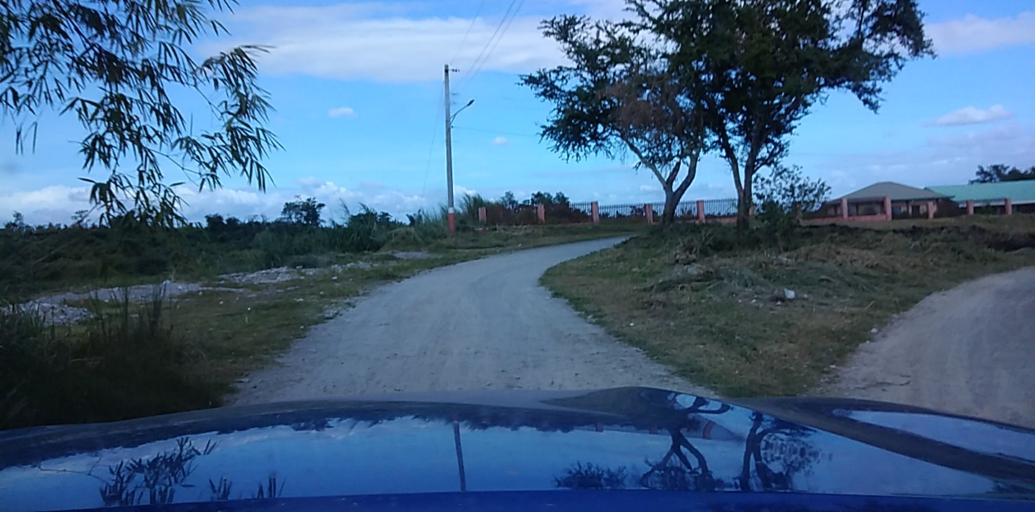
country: PH
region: Central Luzon
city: Santol
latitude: 15.1436
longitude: 120.5227
